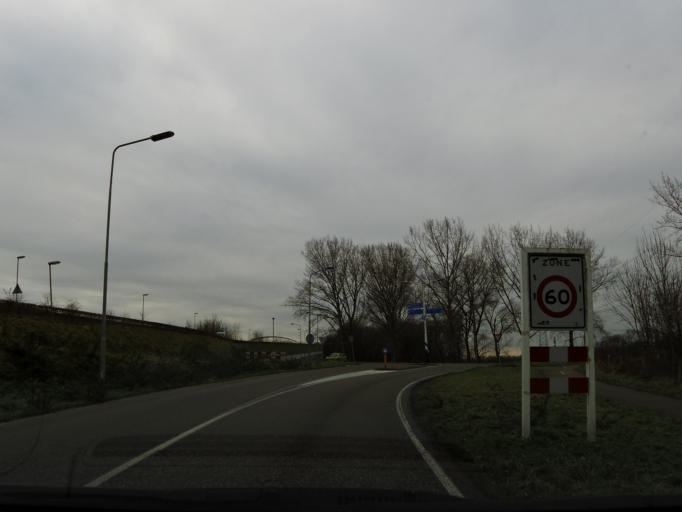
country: NL
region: Limburg
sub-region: Gemeente Maasgouw
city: Maasbracht
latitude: 51.1110
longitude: 5.8518
